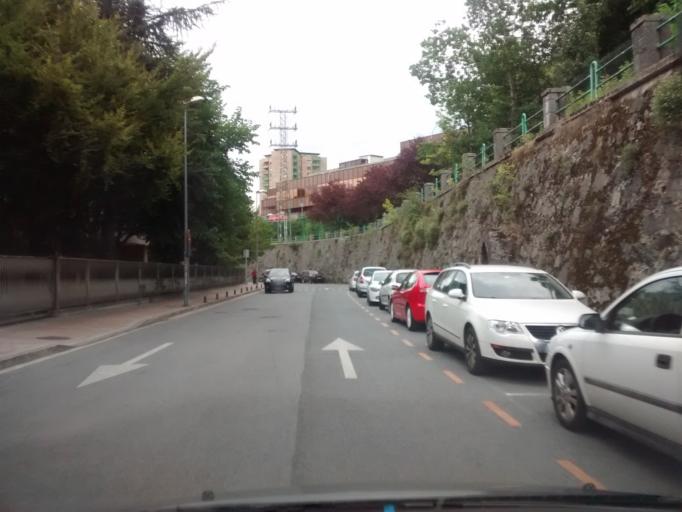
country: ES
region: Basque Country
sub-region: Provincia de Guipuzcoa
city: Arrasate / Mondragon
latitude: 43.0611
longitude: -2.4973
